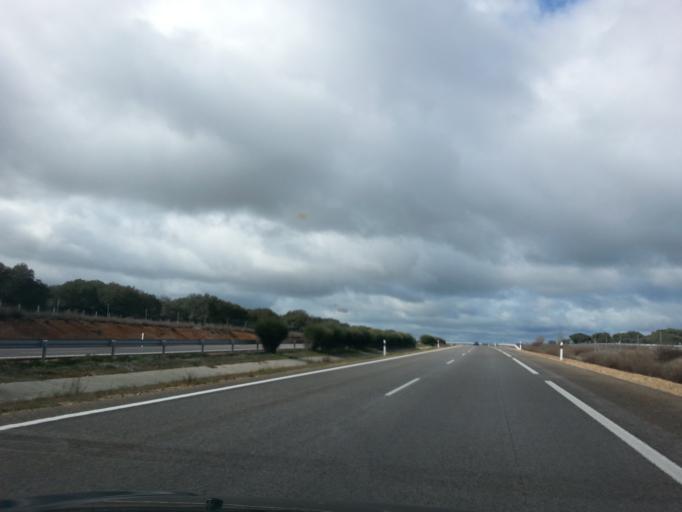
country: ES
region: Castille and Leon
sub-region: Provincia de Salamanca
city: San Munoz
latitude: 40.8088
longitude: -6.1719
